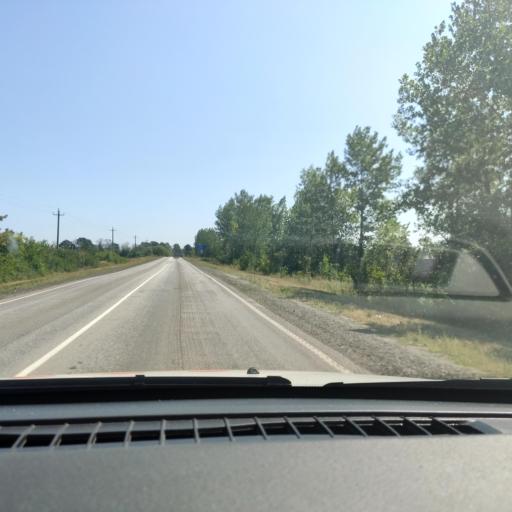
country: RU
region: Voronezj
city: Ostrogozhsk
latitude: 50.8279
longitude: 39.1845
